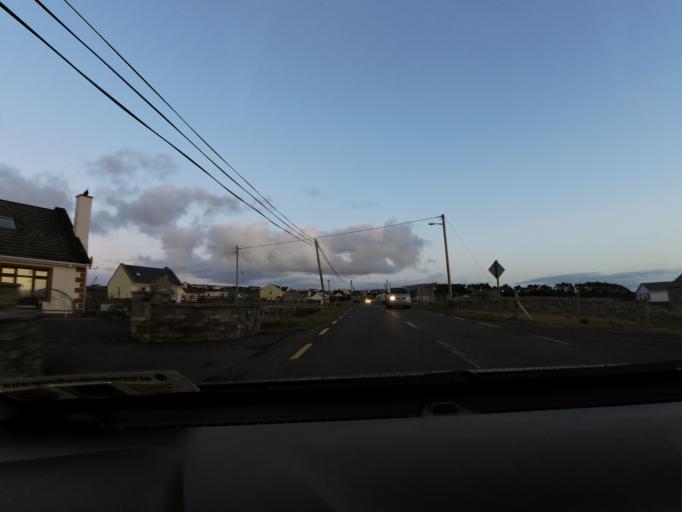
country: IE
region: Connaught
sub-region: Maigh Eo
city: Belmullet
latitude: 53.9749
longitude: -10.1254
